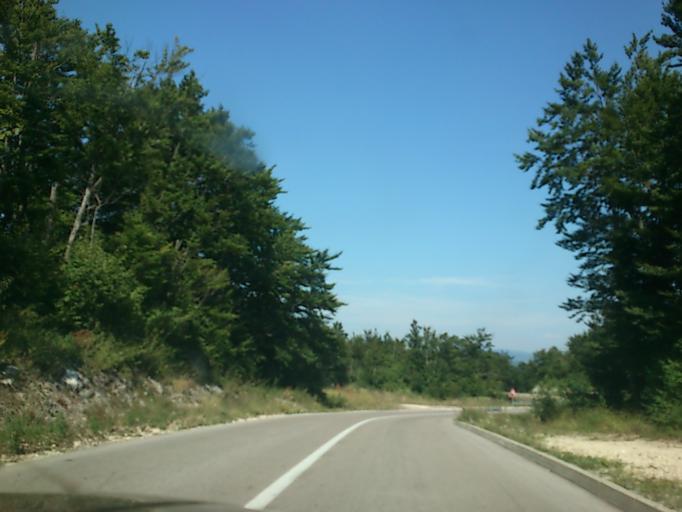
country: HR
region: Licko-Senjska
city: Otocac
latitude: 44.8447
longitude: 15.1208
